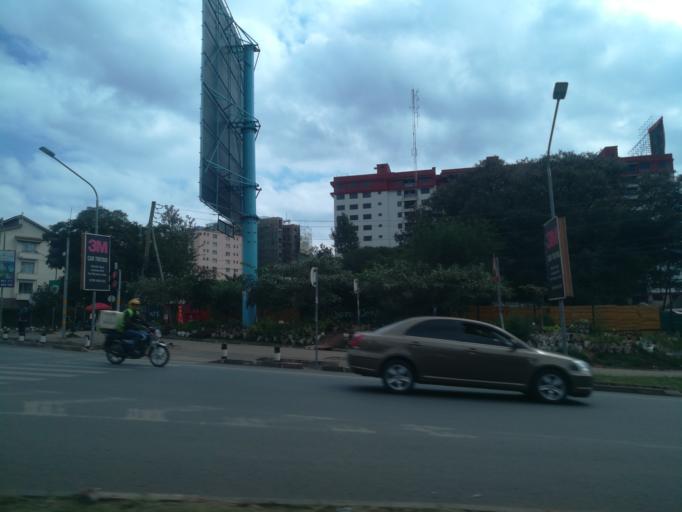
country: KE
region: Nairobi Area
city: Nairobi
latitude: -1.2851
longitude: 36.7880
